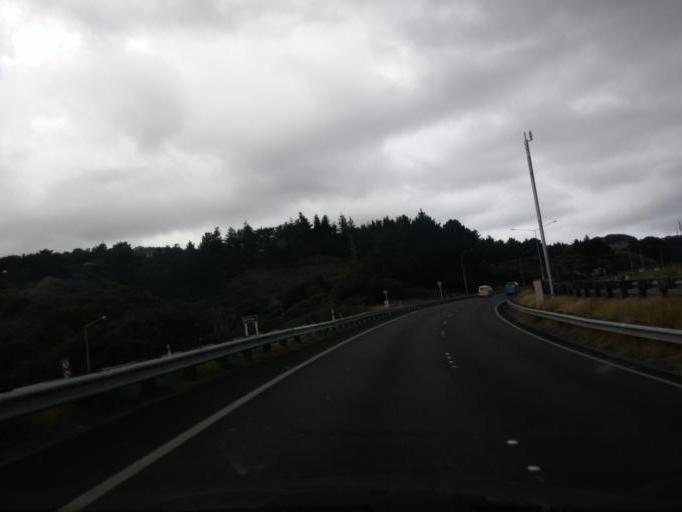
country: NZ
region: Wellington
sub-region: Porirua City
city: Porirua
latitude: -41.1850
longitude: 174.8323
